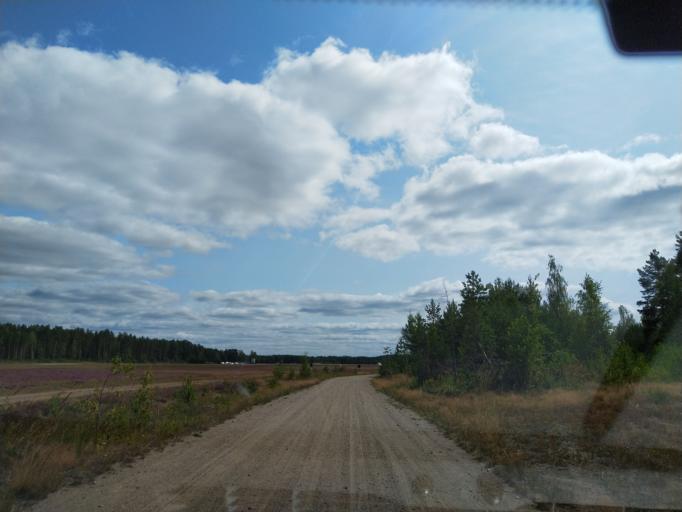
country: FI
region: Uusimaa
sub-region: Helsinki
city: Kaerkoelae
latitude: 60.7485
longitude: 24.1012
